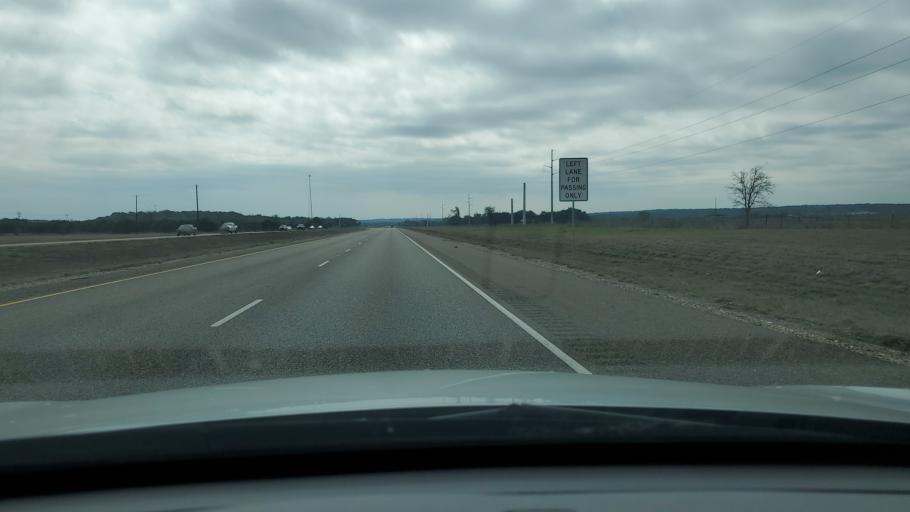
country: US
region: Texas
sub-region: Williamson County
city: Florence
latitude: 30.7844
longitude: -97.7634
